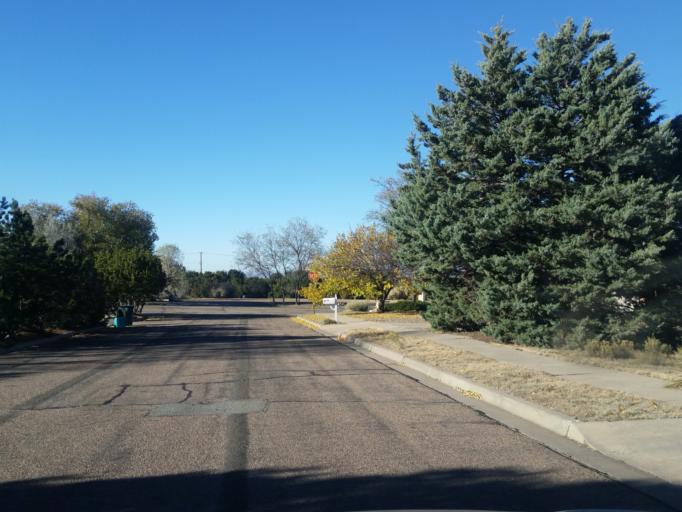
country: US
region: New Mexico
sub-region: Santa Fe County
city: Santa Fe
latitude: 35.6491
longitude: -105.9317
